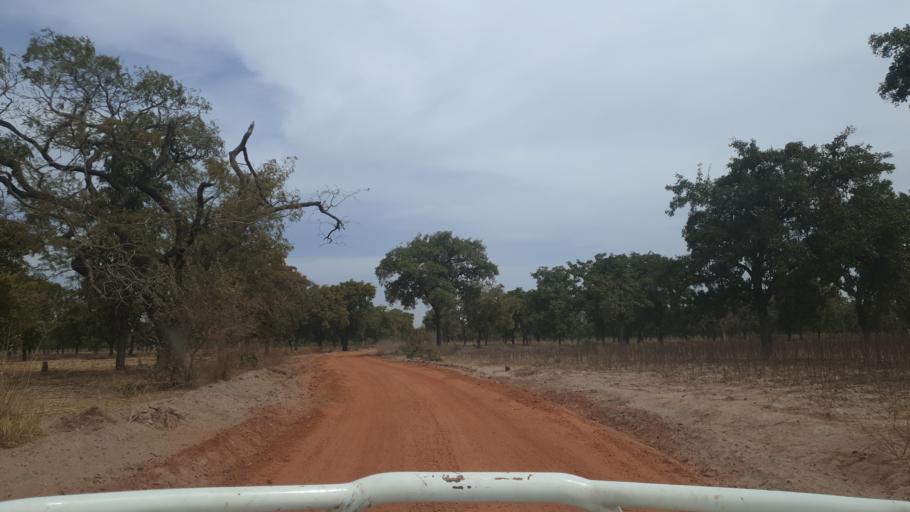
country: ML
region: Sikasso
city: Yorosso
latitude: 12.2315
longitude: -4.7477
